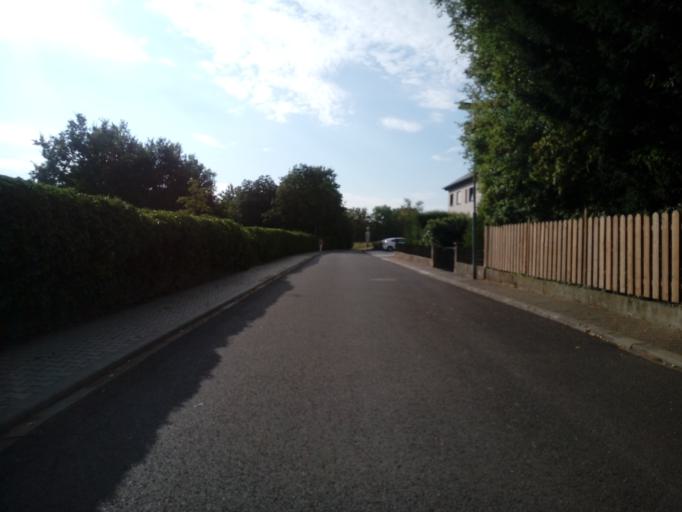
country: DE
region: Rheinland-Pfalz
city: Gutenberg
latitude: 49.8773
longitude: 7.8014
